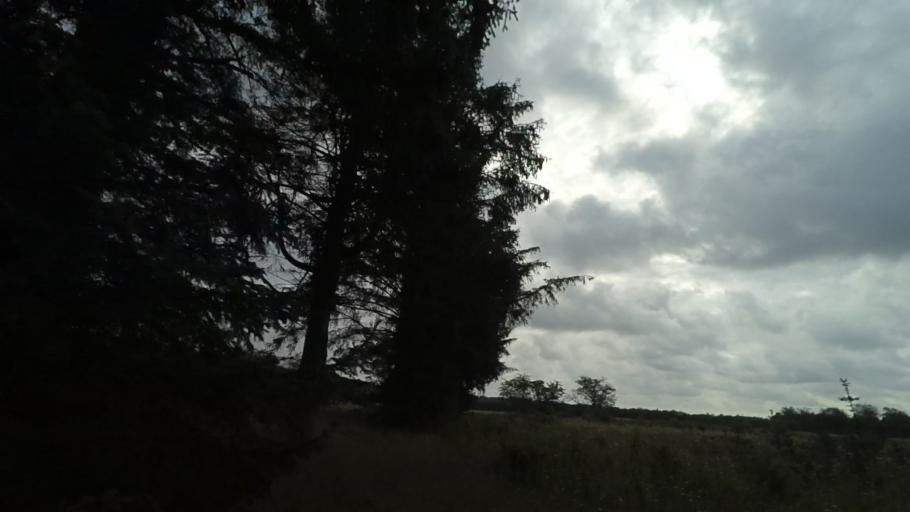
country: DK
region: Central Jutland
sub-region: Syddjurs Kommune
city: Ryomgard
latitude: 56.4436
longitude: 10.5597
